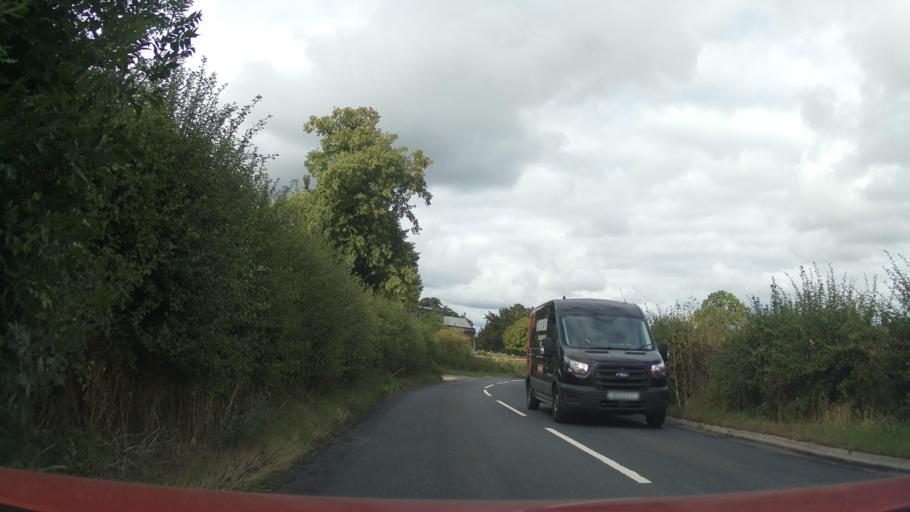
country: GB
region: England
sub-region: Leicestershire
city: Loughborough
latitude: 52.7916
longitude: -1.1969
